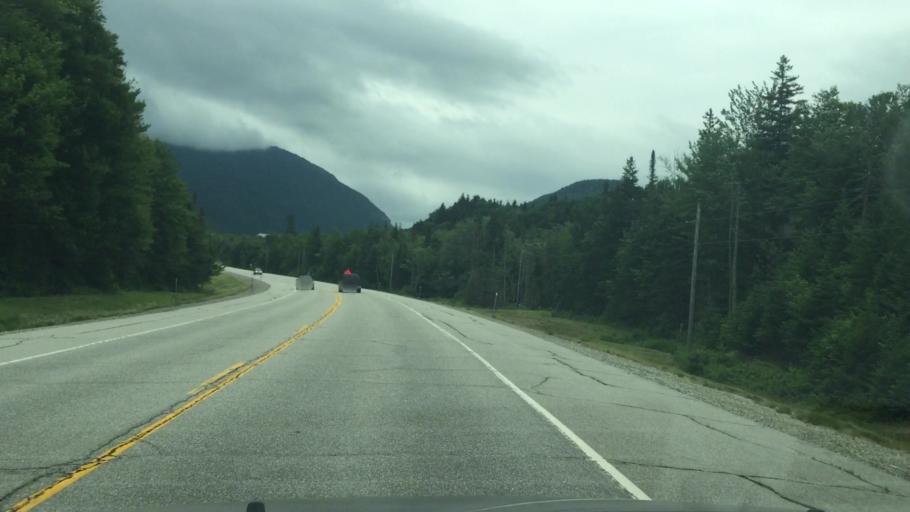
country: US
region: New Hampshire
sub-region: Grafton County
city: Deerfield
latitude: 44.2275
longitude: -71.4187
